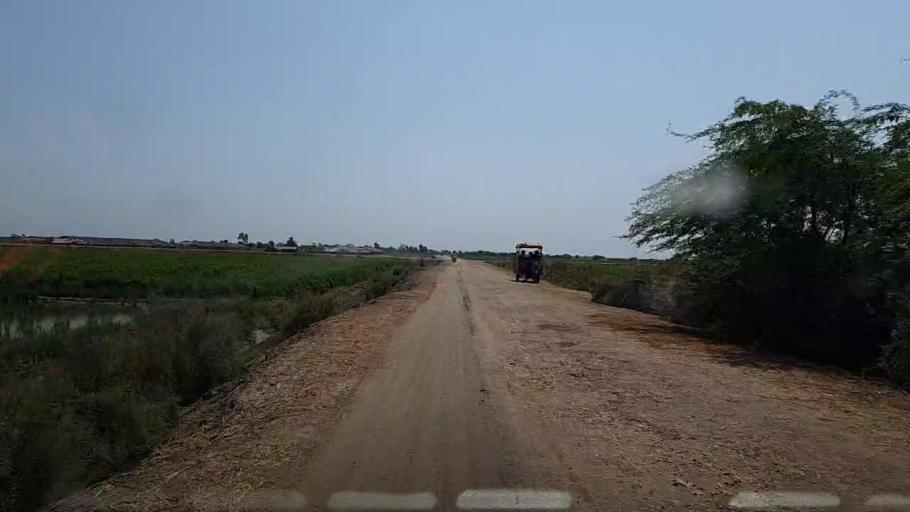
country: PK
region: Sindh
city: Mirpur Batoro
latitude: 24.6230
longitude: 68.4522
